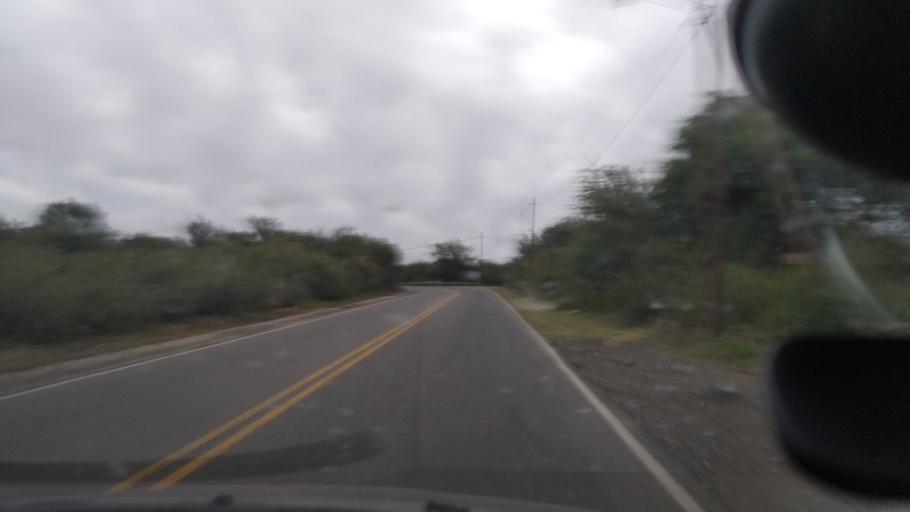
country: AR
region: Cordoba
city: Villa Las Rosas
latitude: -31.9284
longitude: -65.0369
